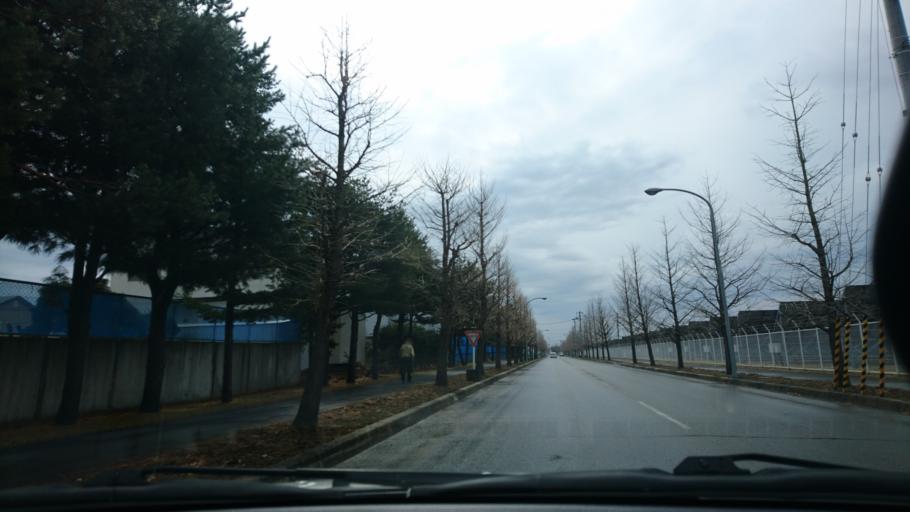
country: JP
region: Hokkaido
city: Otofuke
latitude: 42.9660
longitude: 143.1927
